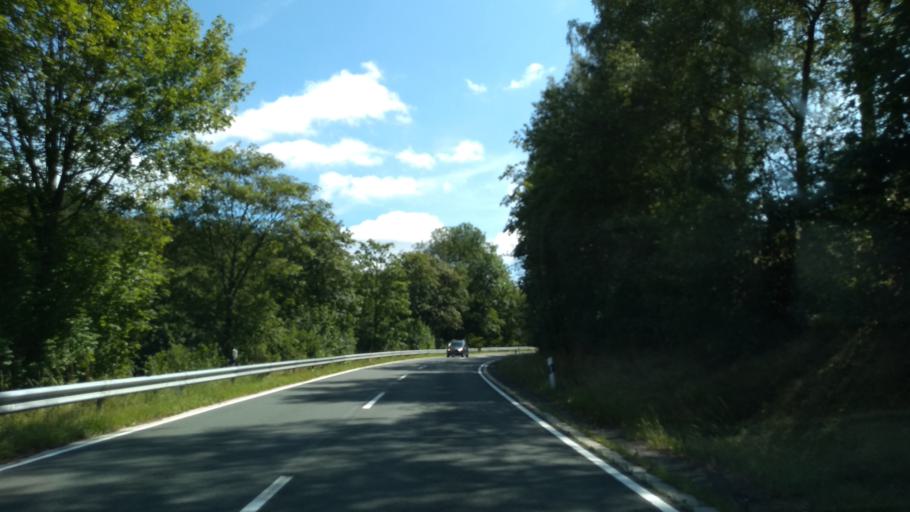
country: DE
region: North Rhine-Westphalia
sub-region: Regierungsbezirk Arnsberg
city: Olpe
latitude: 51.0546
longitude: 7.8562
